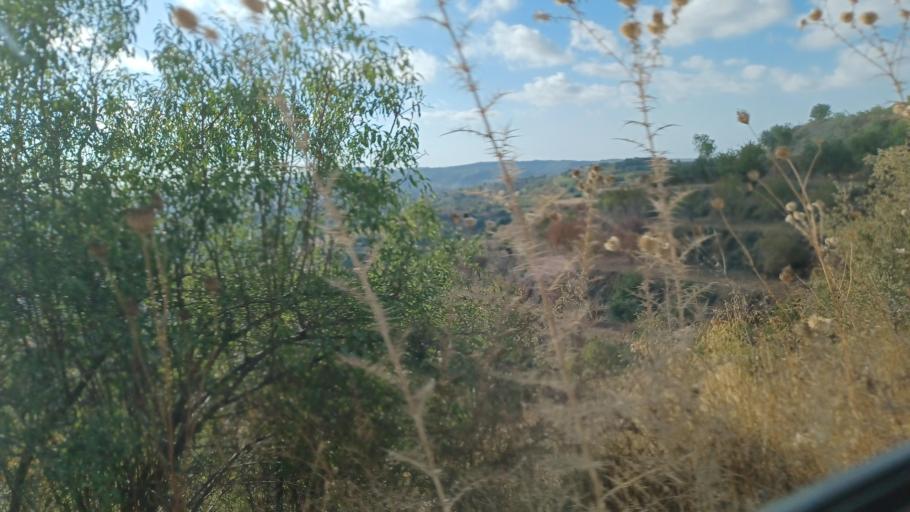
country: CY
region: Pafos
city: Mesogi
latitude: 34.8417
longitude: 32.5251
